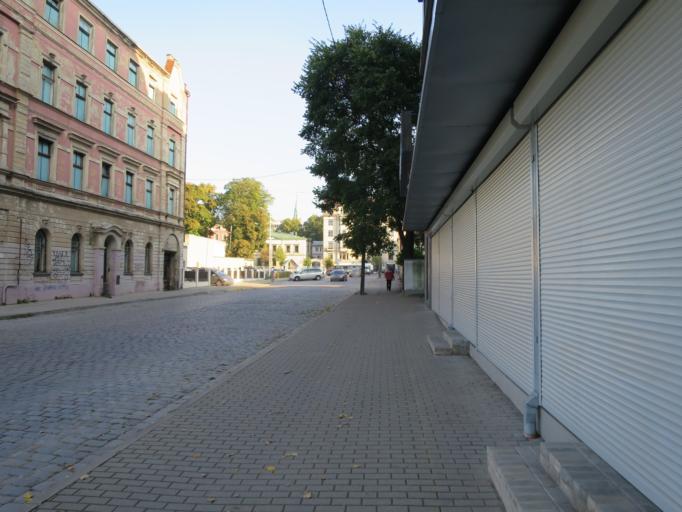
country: LV
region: Riga
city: Riga
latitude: 56.9599
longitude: 24.1165
